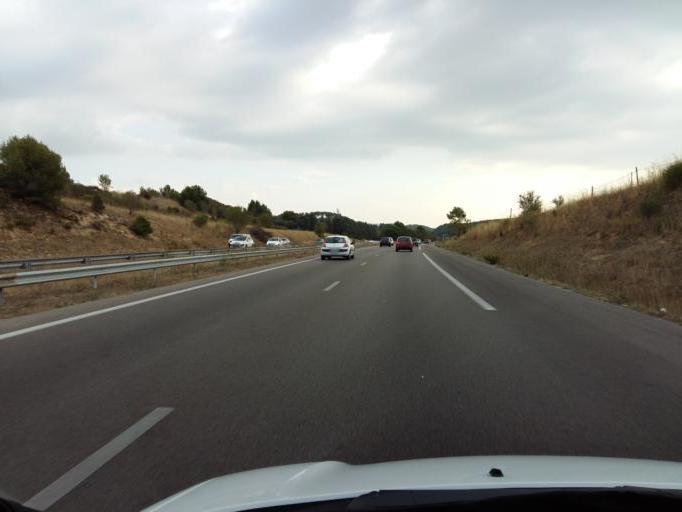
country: FR
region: Provence-Alpes-Cote d'Azur
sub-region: Departement des Bouches-du-Rhone
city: Bouc-Bel-Air
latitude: 43.4800
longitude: 5.4083
